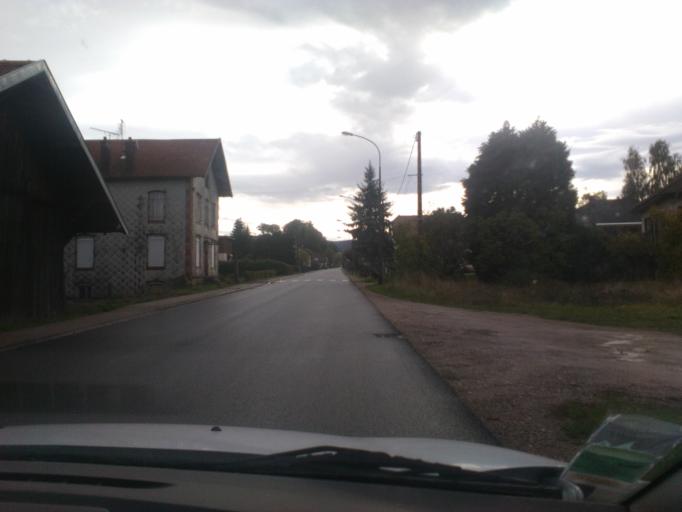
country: FR
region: Lorraine
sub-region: Departement des Vosges
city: Corcieux
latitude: 48.1694
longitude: 6.8865
